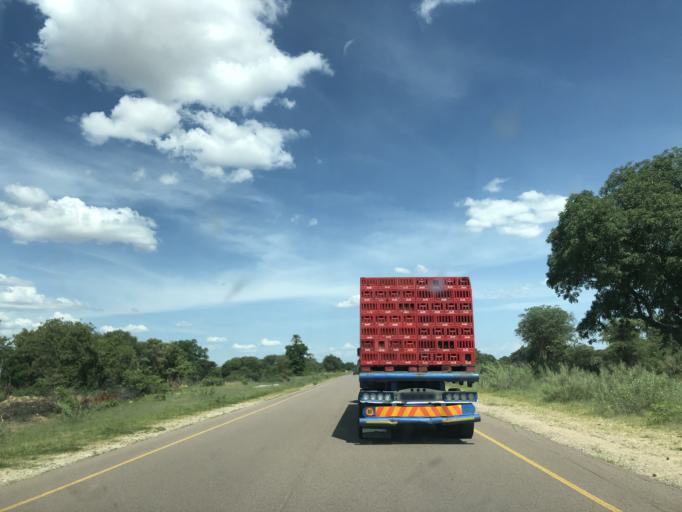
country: AO
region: Cunene
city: Ondjiva
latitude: -16.8946
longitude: 15.5014
